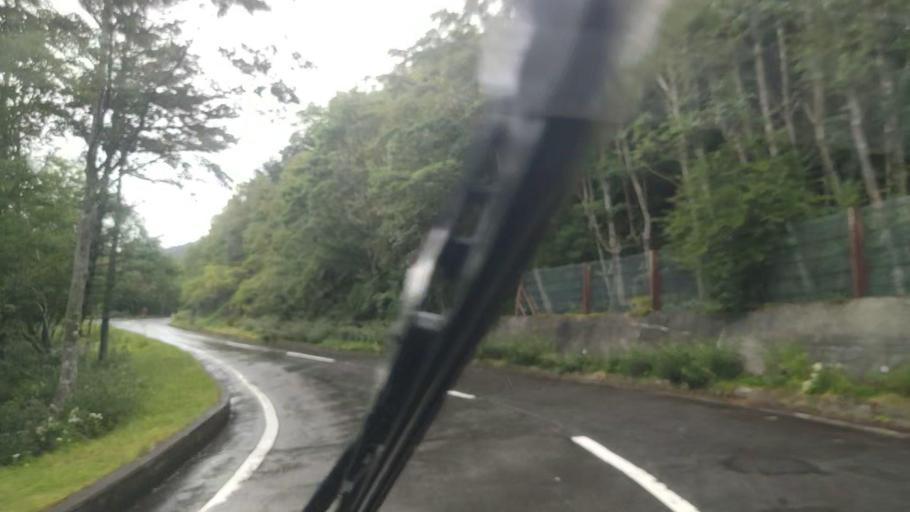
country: JP
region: Shizuoka
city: Fujinomiya
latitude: 35.3290
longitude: 138.7290
